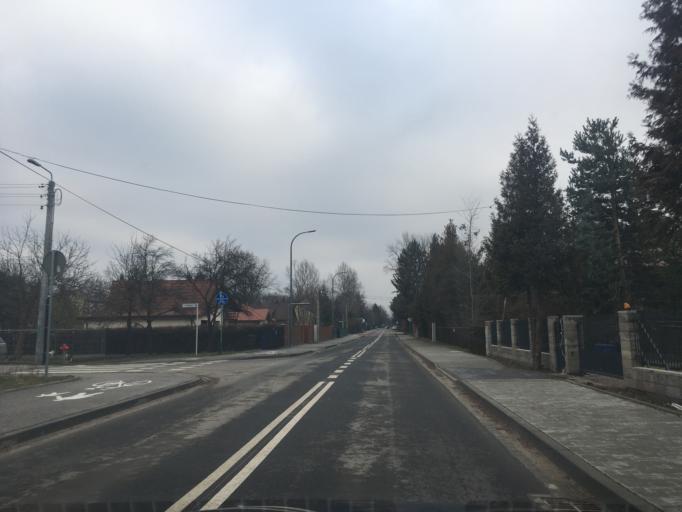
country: PL
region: Masovian Voivodeship
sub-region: Powiat piaseczynski
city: Piaseczno
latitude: 52.0614
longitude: 20.9784
